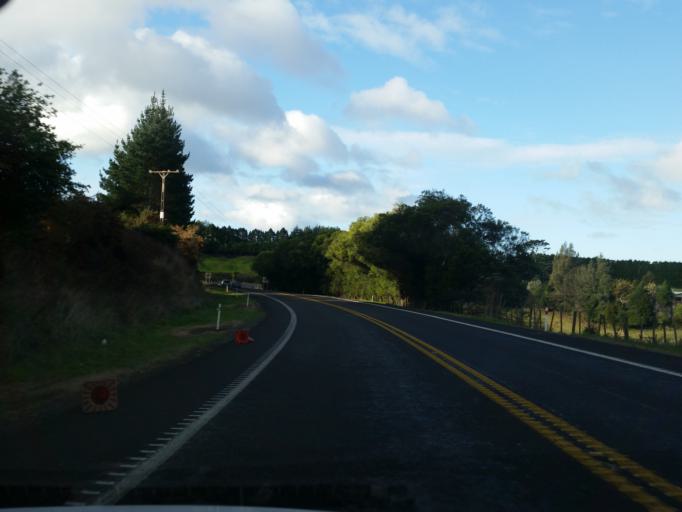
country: NZ
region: Bay of Plenty
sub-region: Western Bay of Plenty District
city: Katikati
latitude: -37.6499
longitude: 175.9719
